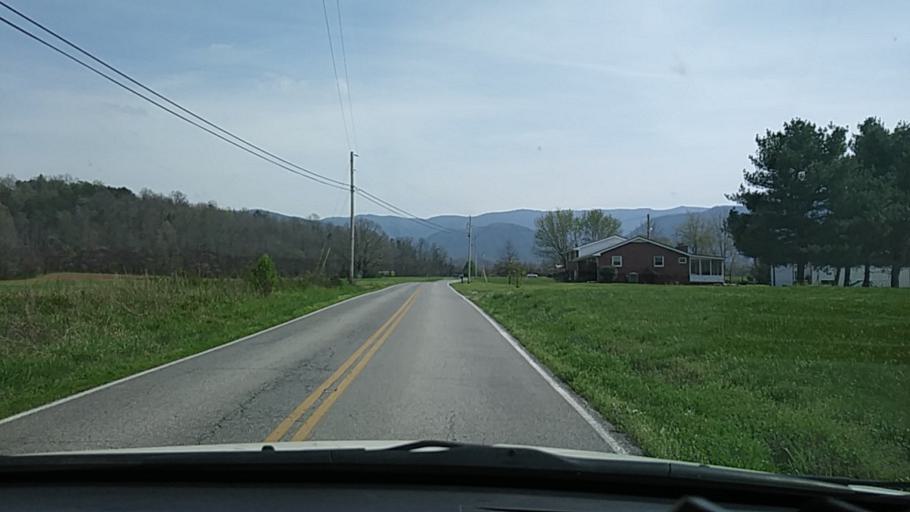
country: US
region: Tennessee
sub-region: Greene County
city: Tusculum
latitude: 36.0993
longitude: -82.7409
